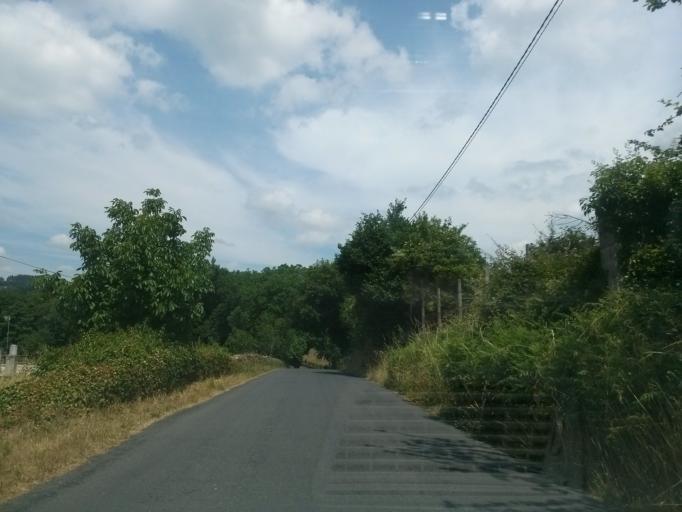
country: ES
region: Galicia
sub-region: Provincia de Lugo
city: Lugo
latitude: 43.0292
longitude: -7.5852
